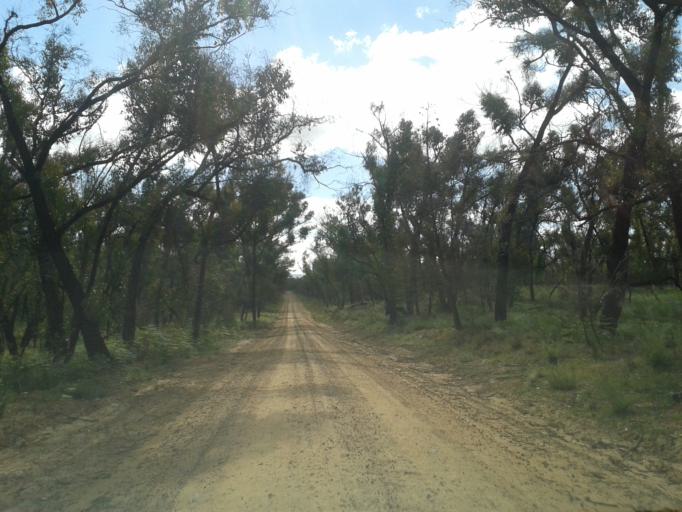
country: AU
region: Victoria
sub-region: Horsham
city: Horsham
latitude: -37.2505
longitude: 142.2565
